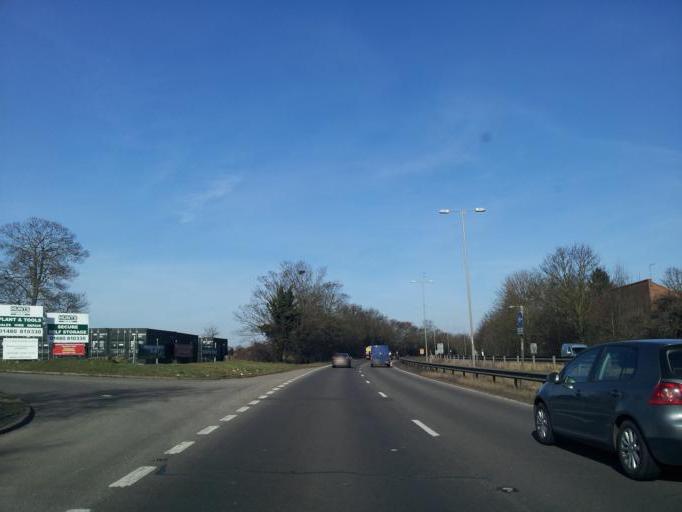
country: GB
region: England
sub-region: Cambridgeshire
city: Buckden
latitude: 52.2933
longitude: -0.2563
